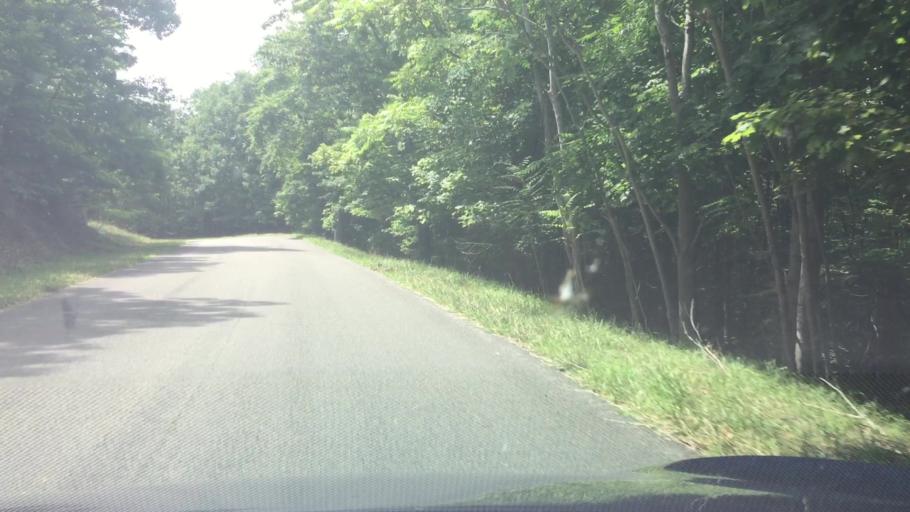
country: US
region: Virginia
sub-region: Wythe County
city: Wytheville
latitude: 36.9254
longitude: -81.0517
